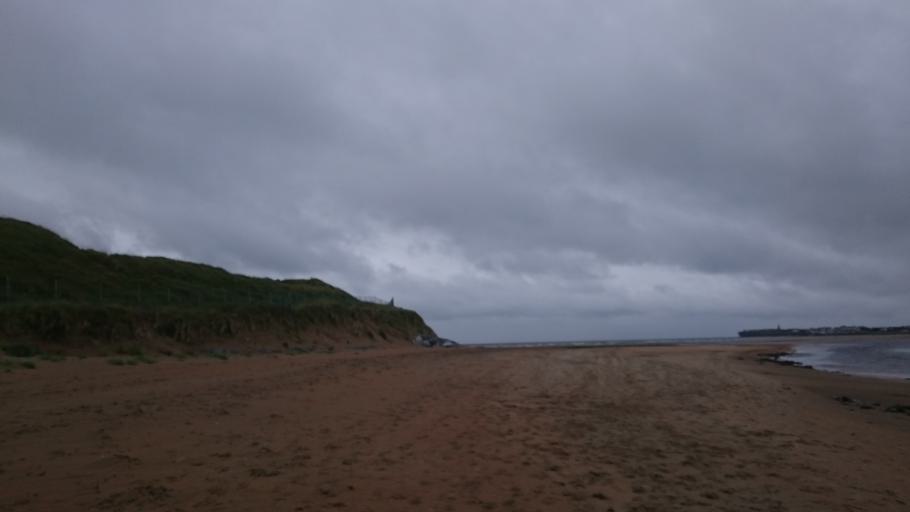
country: IE
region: Munster
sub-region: An Clar
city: Kilrush
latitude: 52.9437
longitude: -9.3567
